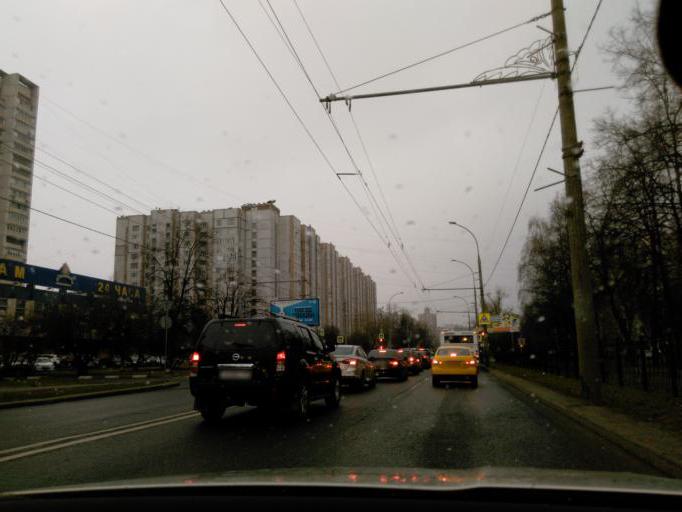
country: RU
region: Moskovskaya
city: Levoberezhnyy
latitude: 55.8484
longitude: 37.4532
